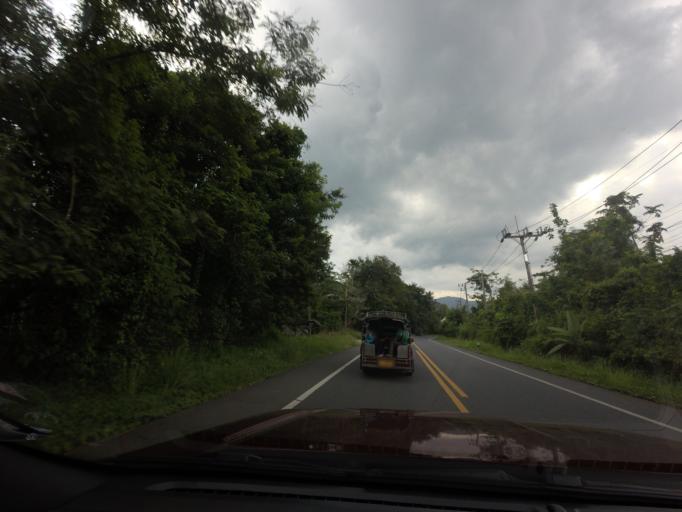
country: TH
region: Yala
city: Than To
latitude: 6.2187
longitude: 101.1651
